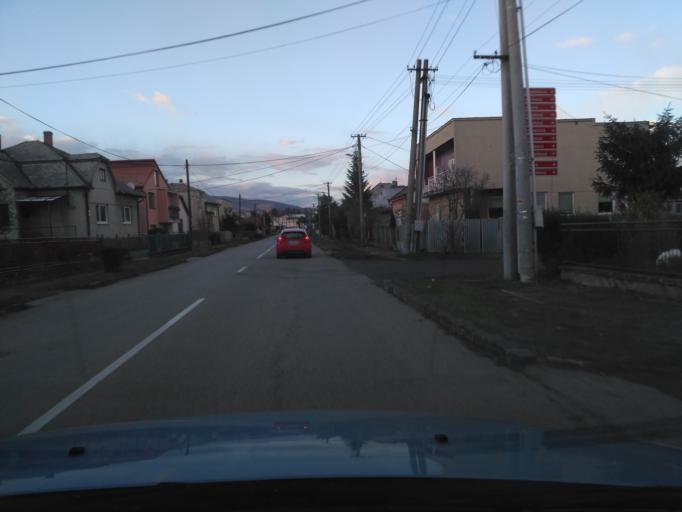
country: SK
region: Kosicky
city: Secovce
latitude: 48.6955
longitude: 21.6518
